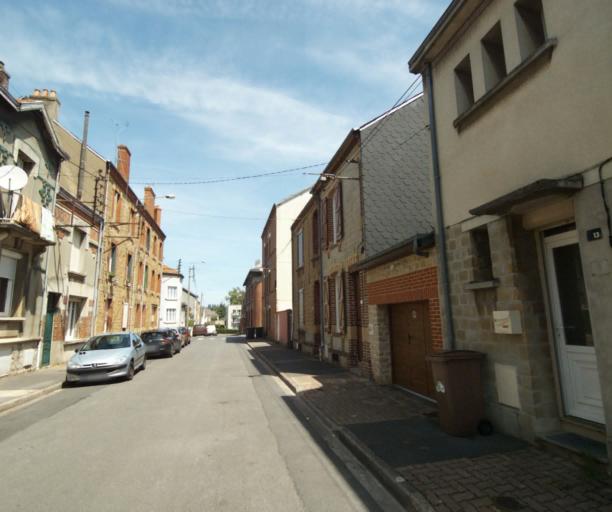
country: FR
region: Champagne-Ardenne
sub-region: Departement des Ardennes
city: Charleville-Mezieres
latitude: 49.7503
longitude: 4.7255
